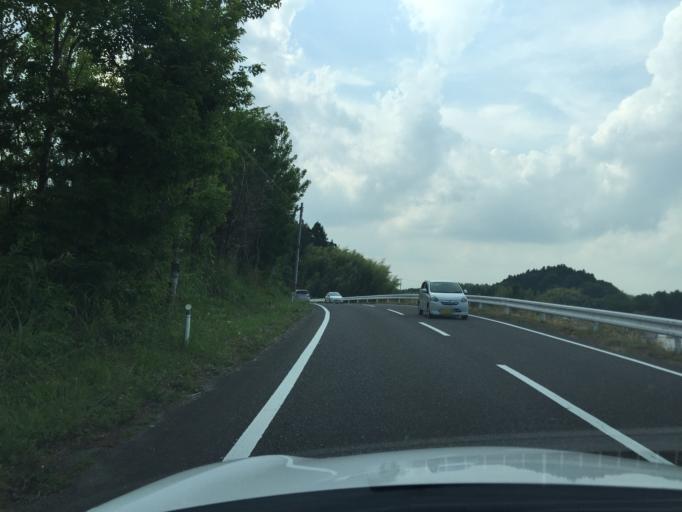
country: JP
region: Fukushima
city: Miharu
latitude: 37.3989
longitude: 140.4465
